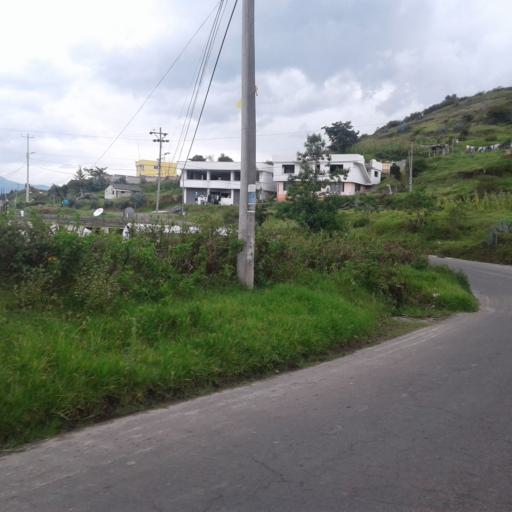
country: EC
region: Pichincha
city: Sangolqui
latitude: -0.2916
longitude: -78.3889
